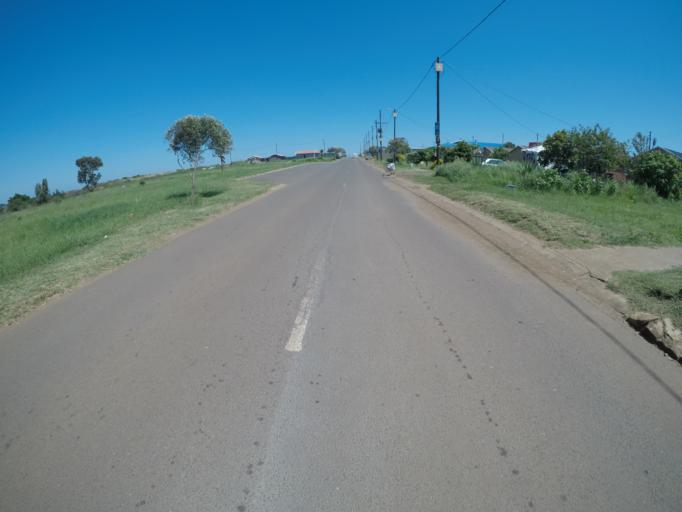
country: ZA
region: KwaZulu-Natal
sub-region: uThungulu District Municipality
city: Empangeni
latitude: -28.7671
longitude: 31.8799
